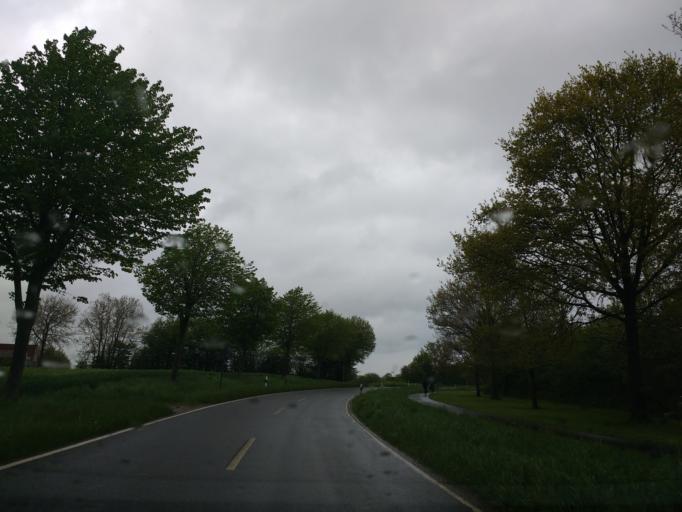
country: DE
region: Schleswig-Holstein
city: Waabs
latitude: 54.5340
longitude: 9.9813
